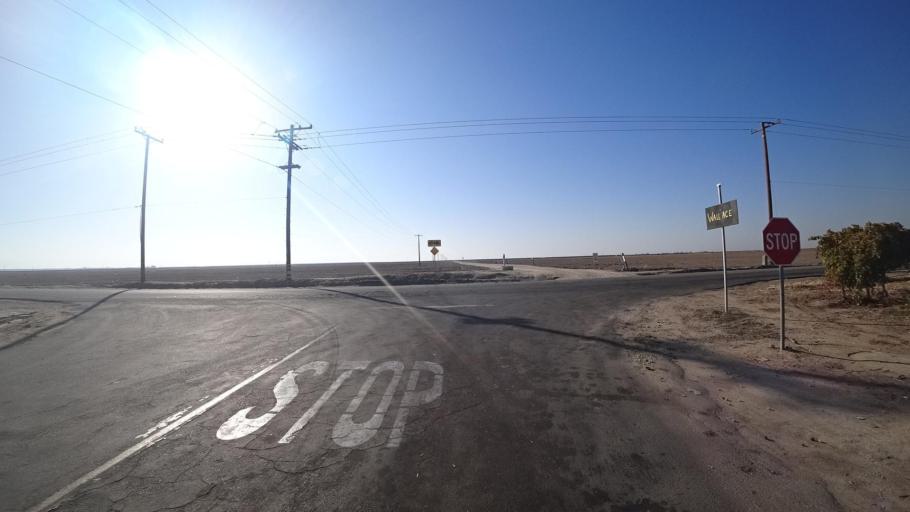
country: US
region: California
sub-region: Kern County
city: McFarland
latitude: 35.7181
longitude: -119.1695
